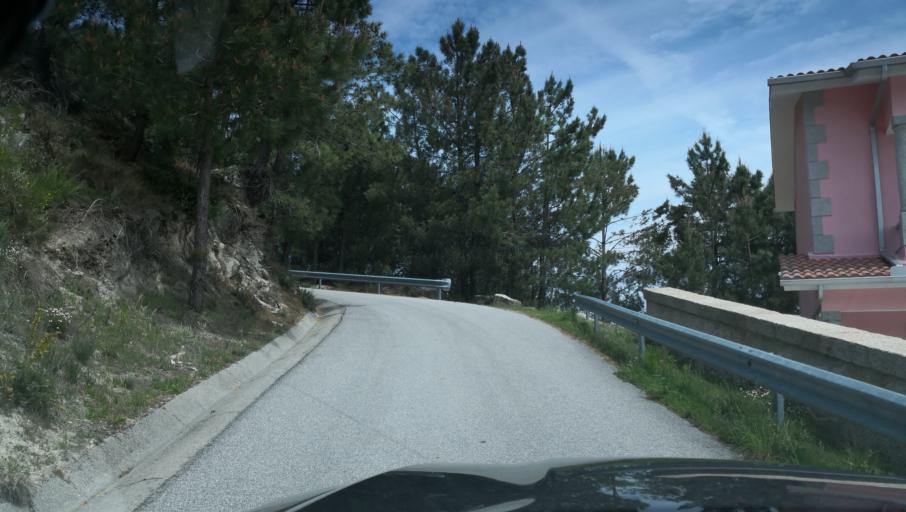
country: PT
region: Vila Real
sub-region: Vila Real
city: Vila Real
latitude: 41.3157
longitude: -7.7957
